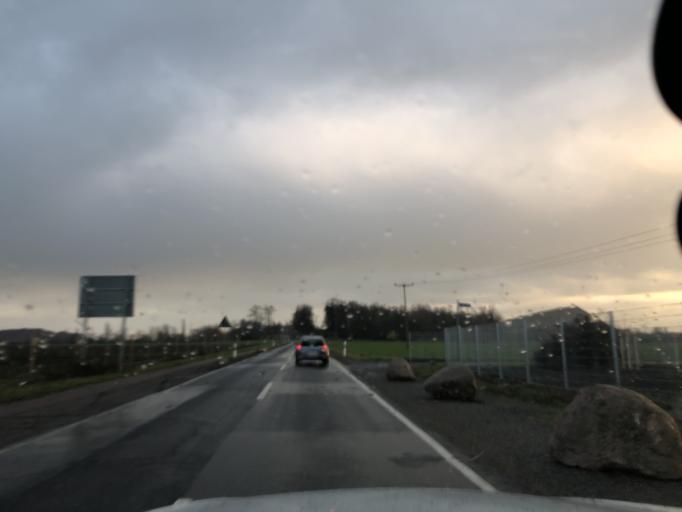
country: DE
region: Saxony-Anhalt
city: Langenbogen
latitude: 51.4770
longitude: 11.7804
